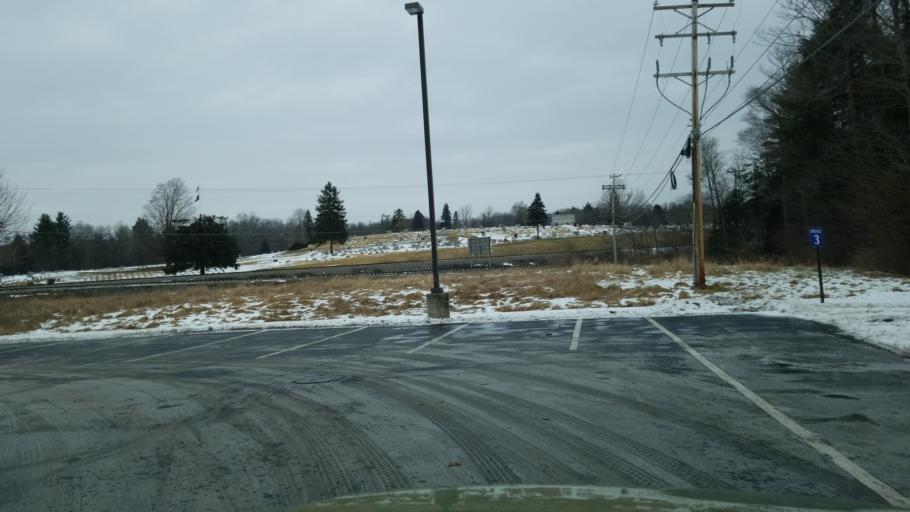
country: US
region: Pennsylvania
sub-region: Clearfield County
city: DuBois
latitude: 41.1218
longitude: -78.7222
